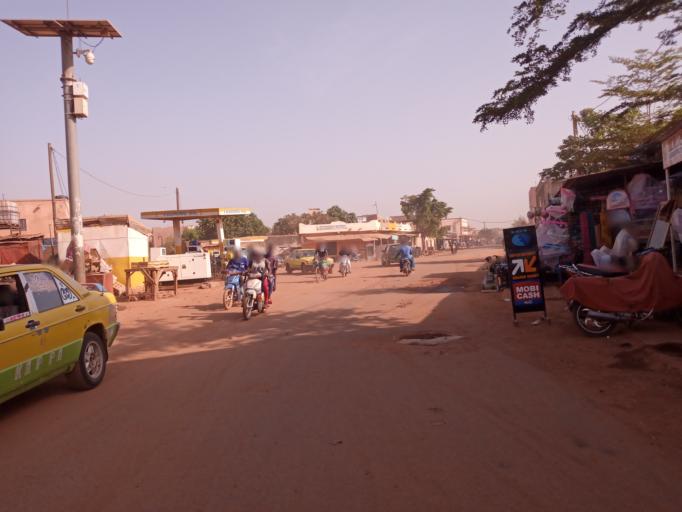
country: ML
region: Bamako
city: Bamako
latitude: 12.5850
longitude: -7.9590
